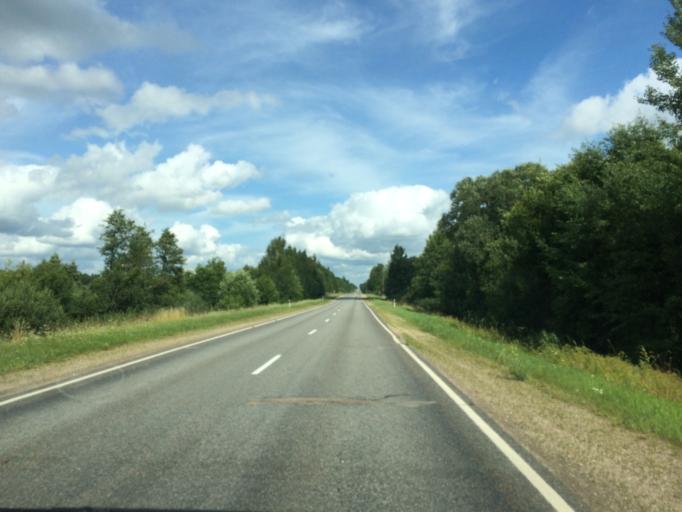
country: LV
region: Rezekne
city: Rezekne
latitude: 56.6389
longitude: 27.4785
